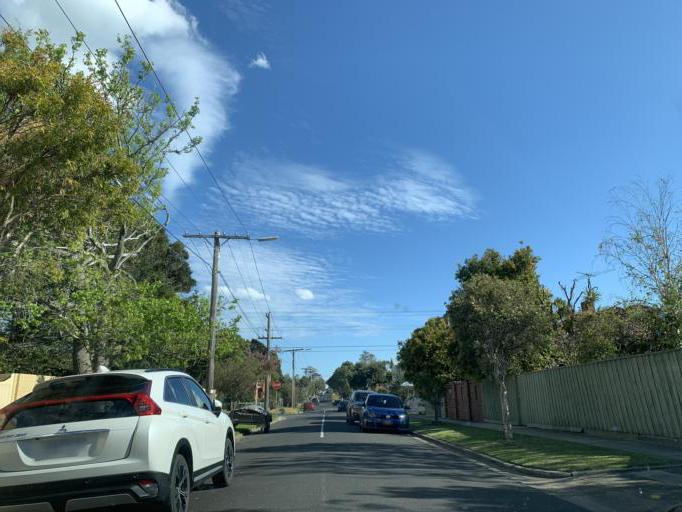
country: AU
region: Victoria
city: Hampton
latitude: -37.9492
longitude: 145.0115
